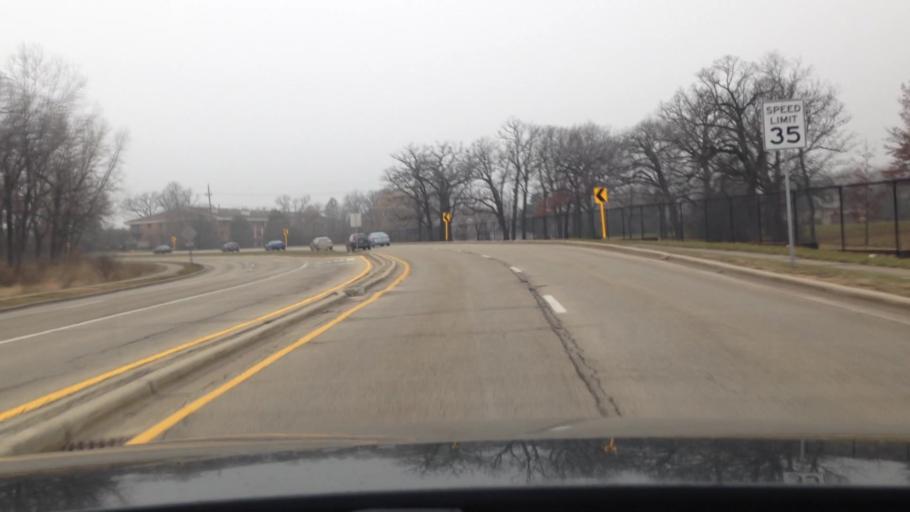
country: US
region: Illinois
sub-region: DuPage County
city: Oakbrook Terrace
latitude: 41.8239
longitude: -87.9743
